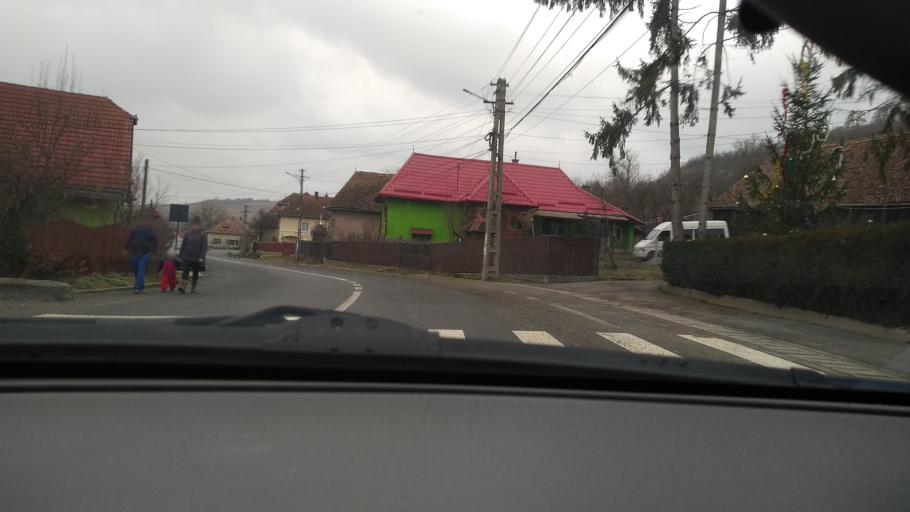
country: RO
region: Mures
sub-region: Comuna Magherani
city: Magherani
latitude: 46.5640
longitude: 24.9108
